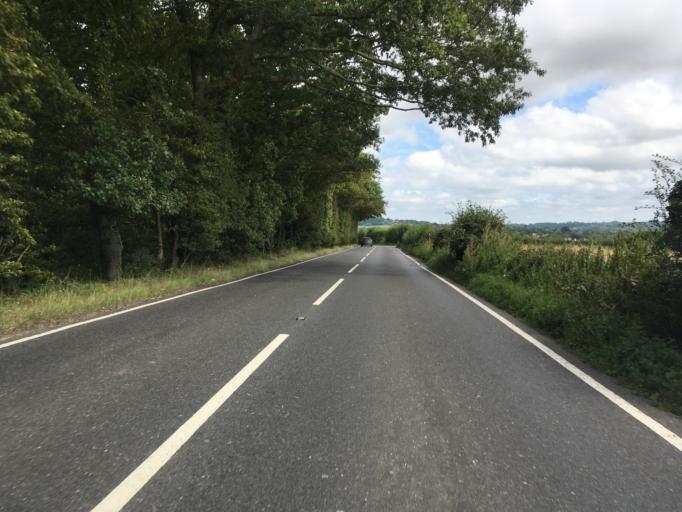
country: GB
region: England
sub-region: Kent
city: Paddock Wood
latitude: 51.1100
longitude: 0.4230
